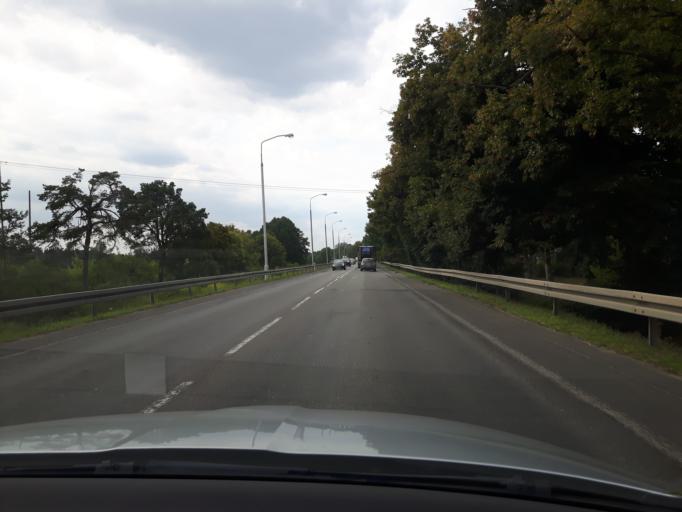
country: PL
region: Masovian Voivodeship
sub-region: Powiat legionowski
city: Nieporet
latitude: 52.4416
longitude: 21.0132
